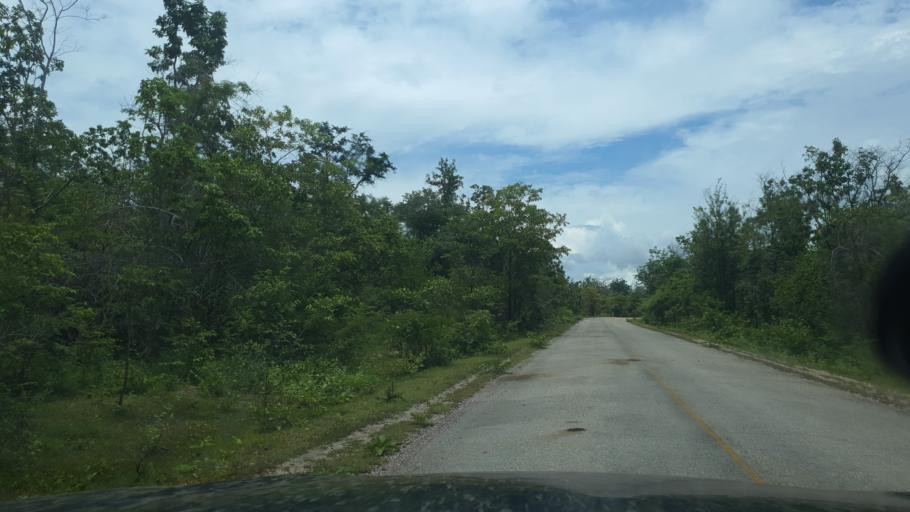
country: TH
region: Lampang
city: Soem Ngam
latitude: 18.0539
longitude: 99.3634
